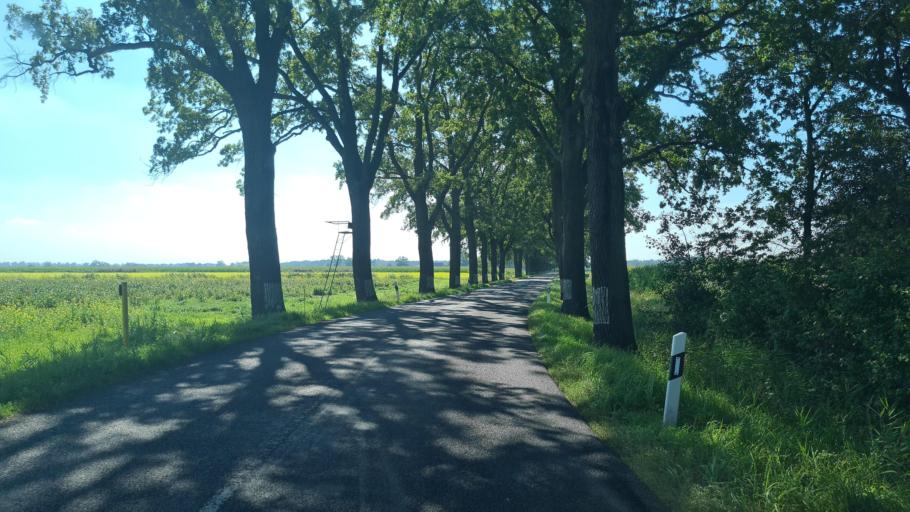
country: DE
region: Brandenburg
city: Paulinenaue
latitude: 52.6569
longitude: 12.7057
